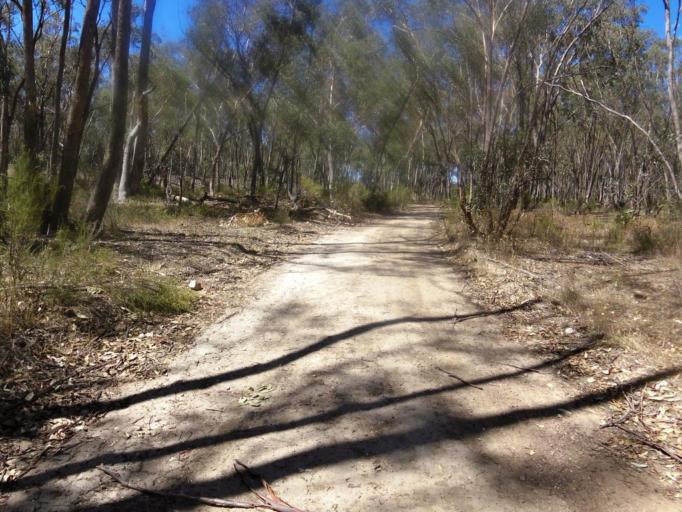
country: AU
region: Victoria
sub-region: Mount Alexander
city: Castlemaine
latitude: -37.0530
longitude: 144.1859
